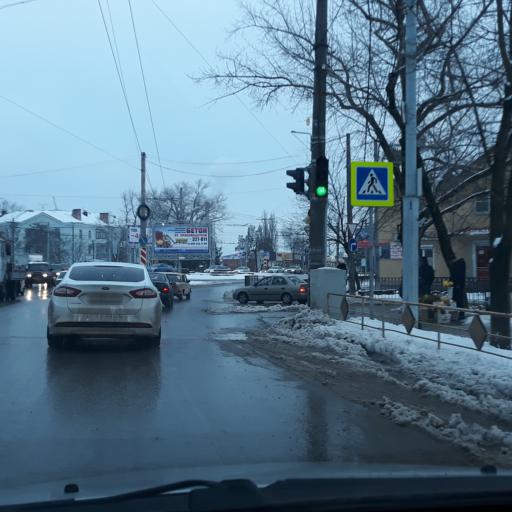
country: RU
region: Rostov
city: Taganrog
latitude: 47.2412
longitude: 38.8844
